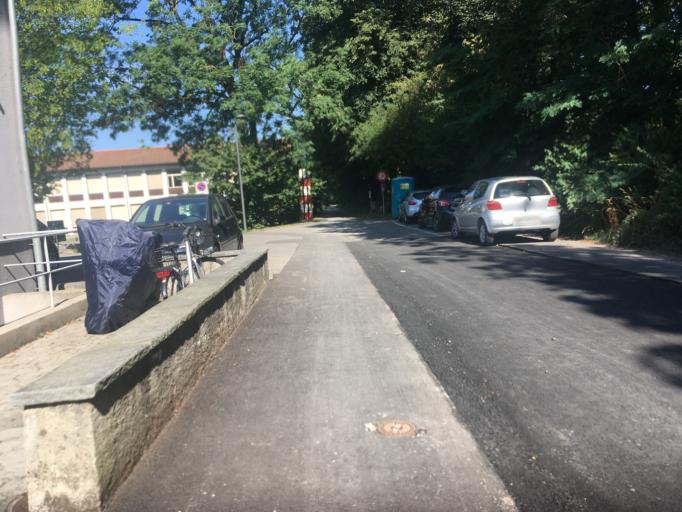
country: CH
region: Bern
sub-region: Emmental District
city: Burgdorf
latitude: 47.0653
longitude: 7.6175
